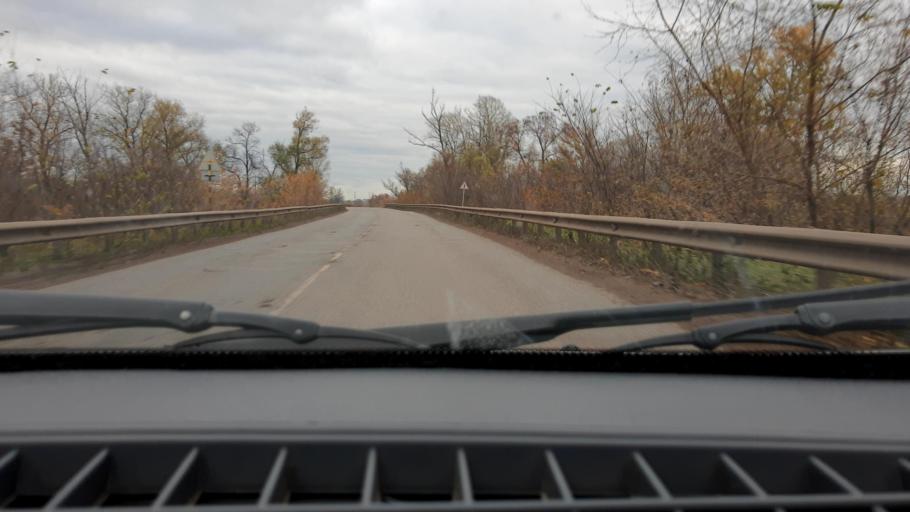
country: RU
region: Bashkortostan
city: Ufa
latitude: 54.5683
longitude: 55.9785
